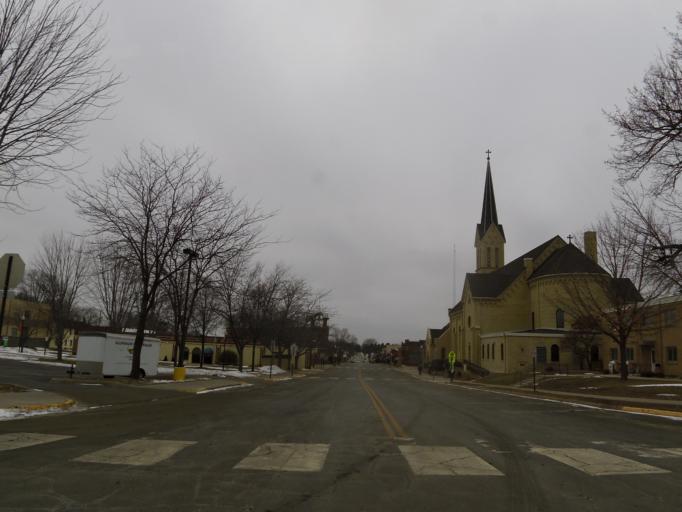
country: US
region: Minnesota
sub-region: Carver County
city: Waconia
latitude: 44.8494
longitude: -93.7846
